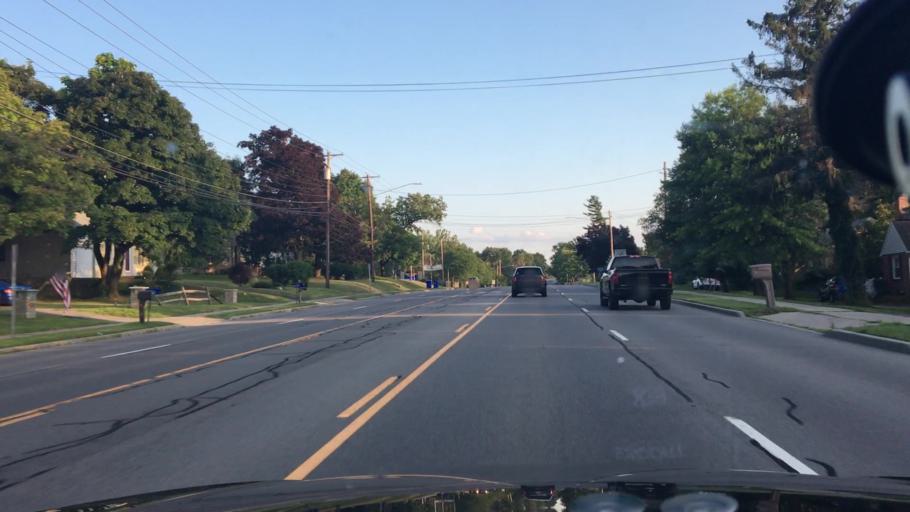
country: US
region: New York
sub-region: Erie County
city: Orchard Park
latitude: 42.8148
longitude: -78.7523
